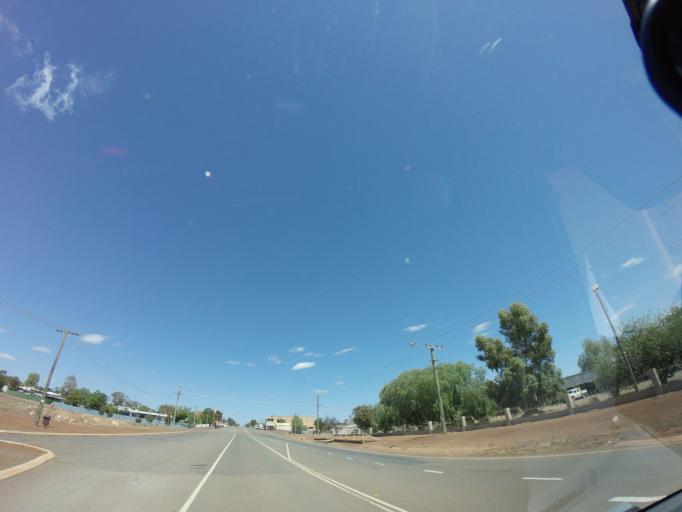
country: AU
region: Western Australia
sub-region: Kalgoorlie/Boulder
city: Boulder
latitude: -30.9547
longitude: 121.1714
